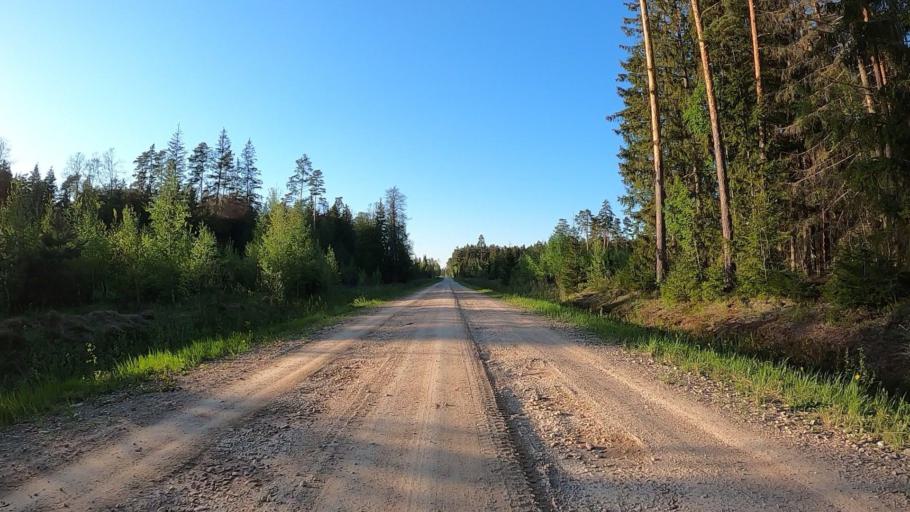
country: LV
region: Kekava
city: Kekava
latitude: 56.7634
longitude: 24.2227
